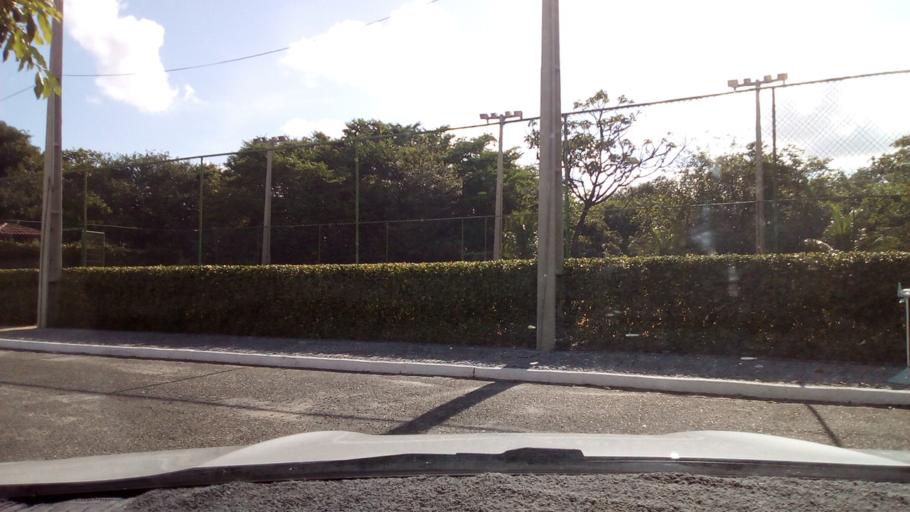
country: BR
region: Paraiba
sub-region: Joao Pessoa
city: Joao Pessoa
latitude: -7.1563
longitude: -34.8088
